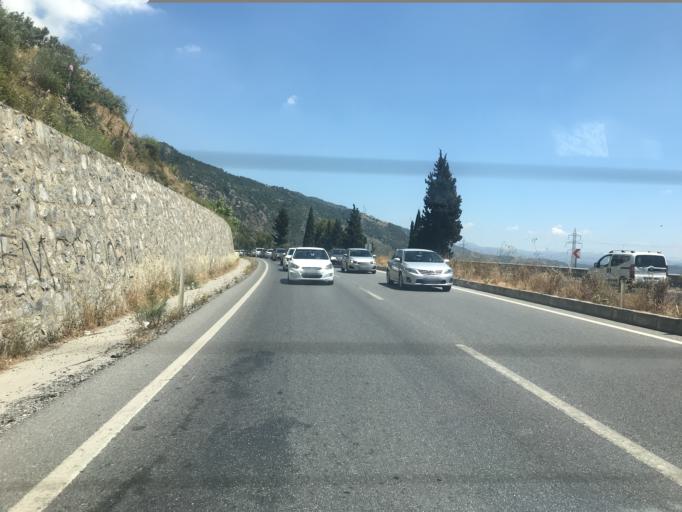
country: TR
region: Aydin
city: Soeke
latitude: 37.7883
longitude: 27.4662
